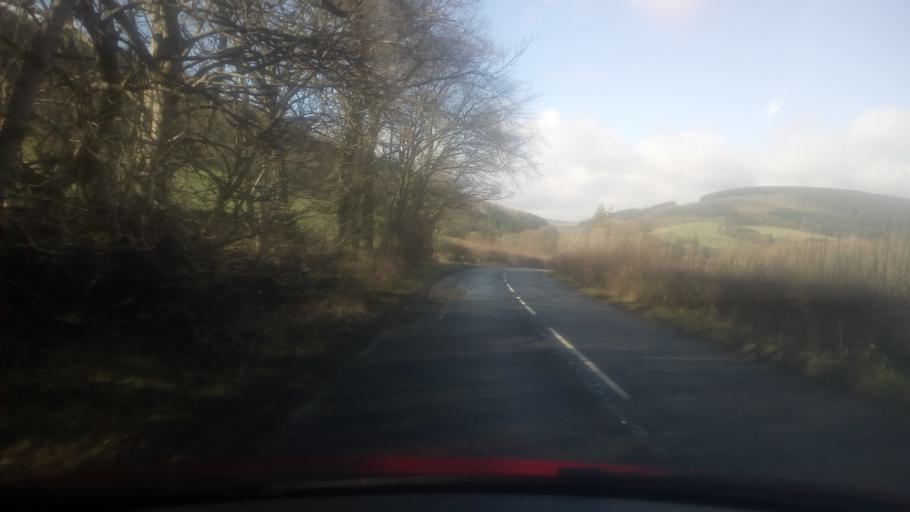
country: GB
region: Scotland
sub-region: The Scottish Borders
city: Selkirk
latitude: 55.5818
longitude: -2.8476
